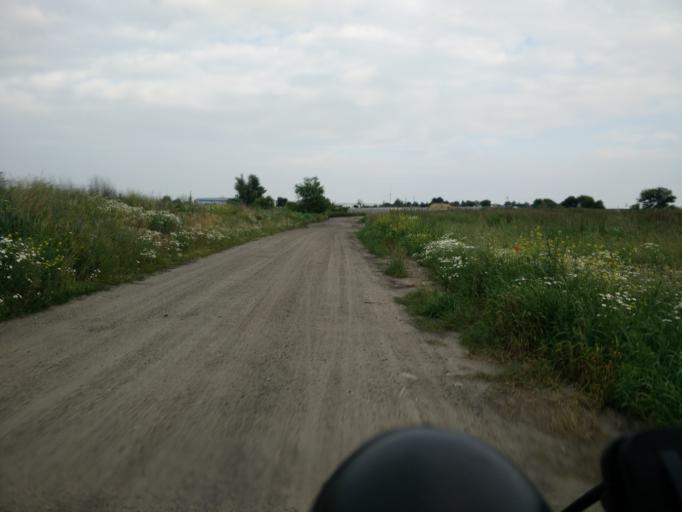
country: PL
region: Greater Poland Voivodeship
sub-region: Powiat sredzki
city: Sroda Wielkopolska
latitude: 52.2133
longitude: 17.2914
